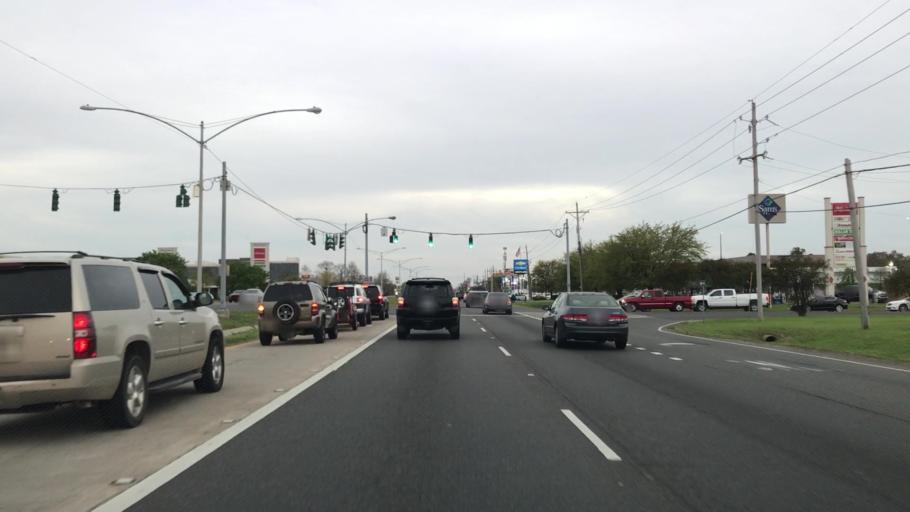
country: US
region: Louisiana
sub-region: Bossier Parish
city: Bossier City
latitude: 32.4388
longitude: -93.7161
